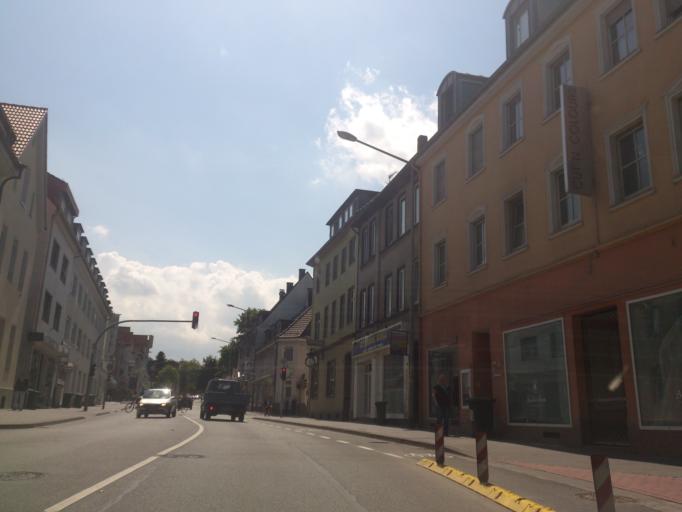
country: DE
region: North Rhine-Westphalia
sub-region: Regierungsbezirk Detmold
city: Paderborn
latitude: 51.7135
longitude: 8.7456
